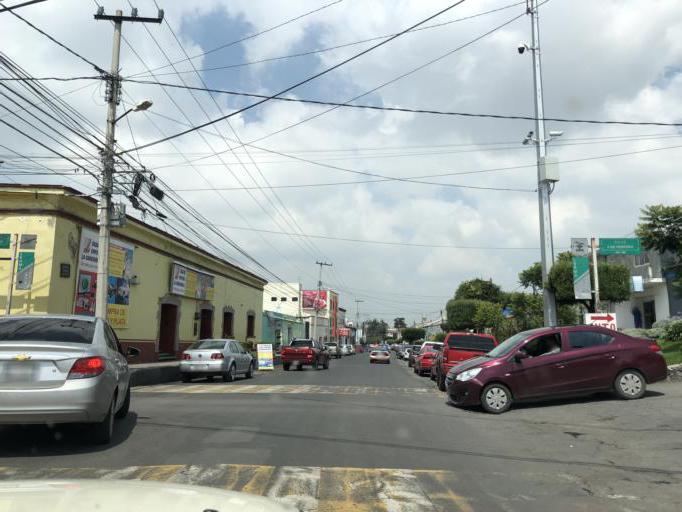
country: MX
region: Morelos
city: Lerma de Villada
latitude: 19.2865
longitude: -99.5126
